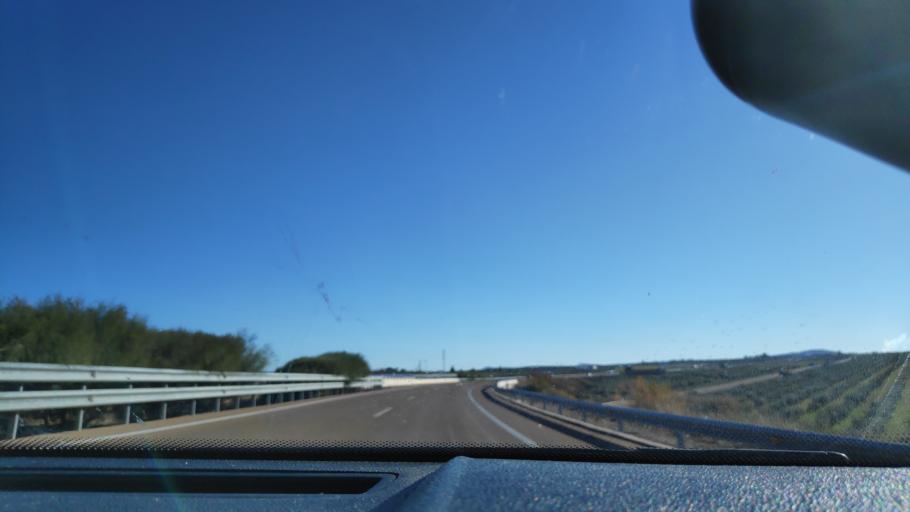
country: ES
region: Extremadura
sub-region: Provincia de Badajoz
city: Villafranca de los Barros
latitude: 38.5278
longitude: -6.3508
